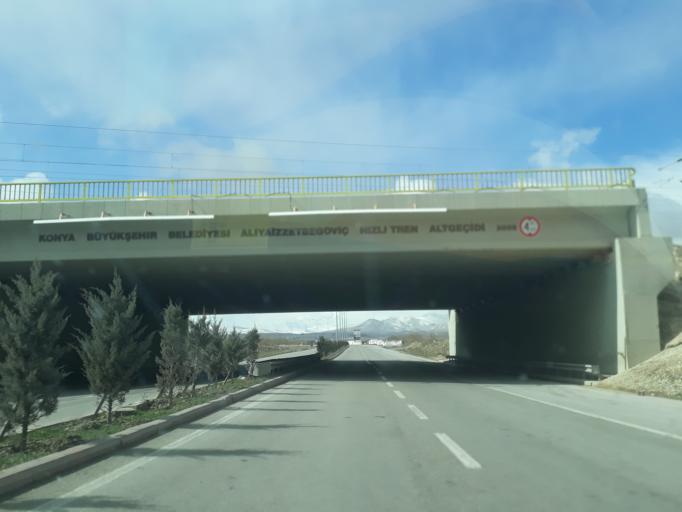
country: TR
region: Konya
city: Asagipinarbasi
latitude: 37.9951
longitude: 32.5882
